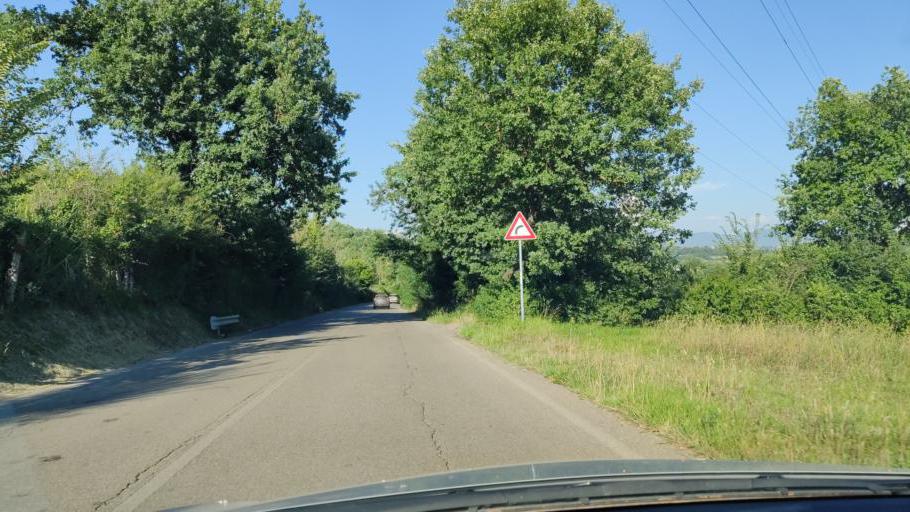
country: IT
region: Latium
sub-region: Provincia di Viterbo
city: Orte
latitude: 42.4696
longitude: 12.3801
